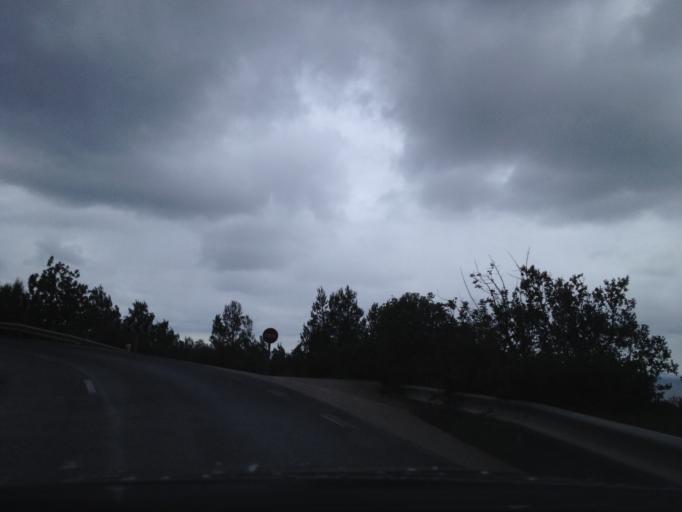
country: ES
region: Balearic Islands
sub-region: Illes Balears
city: Deia
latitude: 39.7579
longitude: 2.6481
